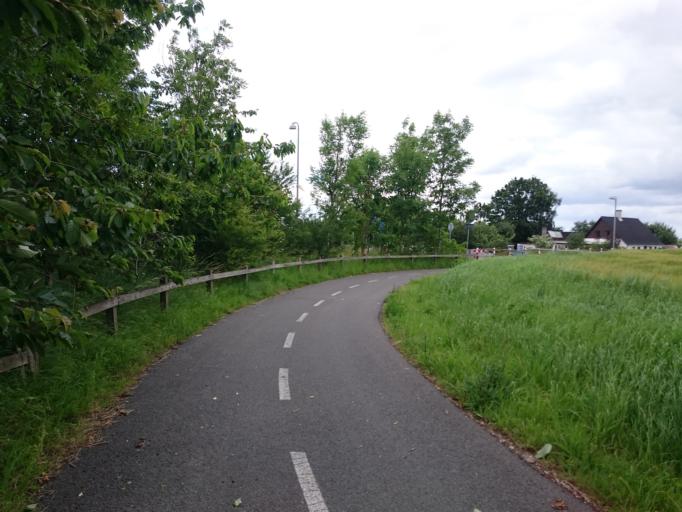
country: DK
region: South Denmark
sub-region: Faaborg-Midtfyn Kommune
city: Arslev
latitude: 55.3409
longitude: 10.5032
